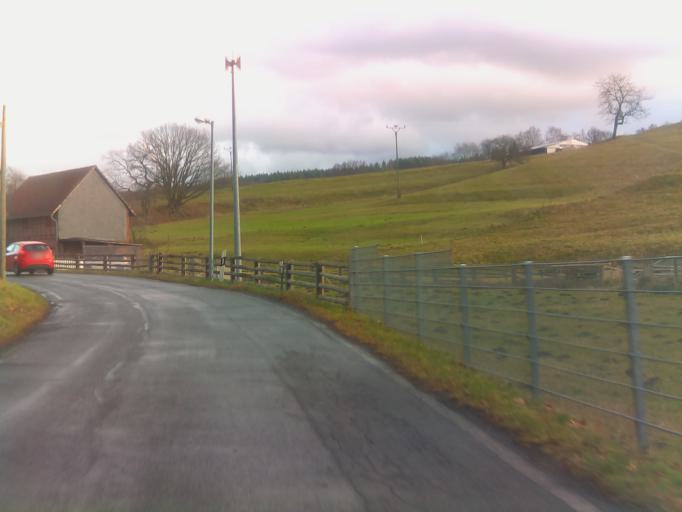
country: DE
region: Thuringia
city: Unterwellenborn
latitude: 50.6883
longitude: 11.4260
